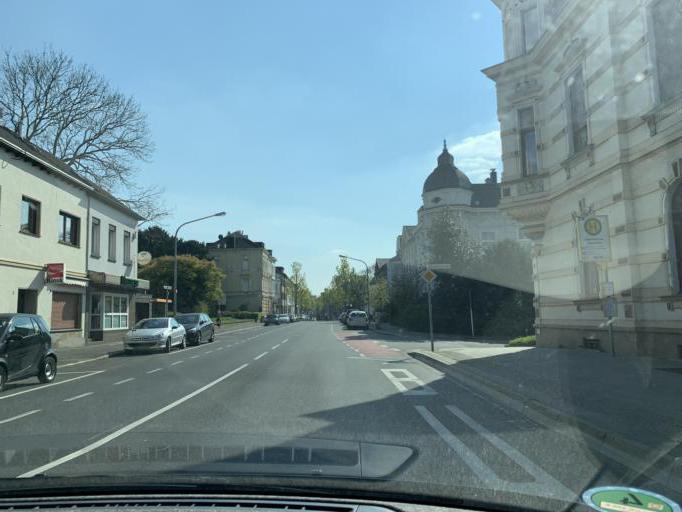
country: DE
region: North Rhine-Westphalia
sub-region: Regierungsbezirk Dusseldorf
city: Monchengladbach
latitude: 51.1376
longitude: 6.4537
